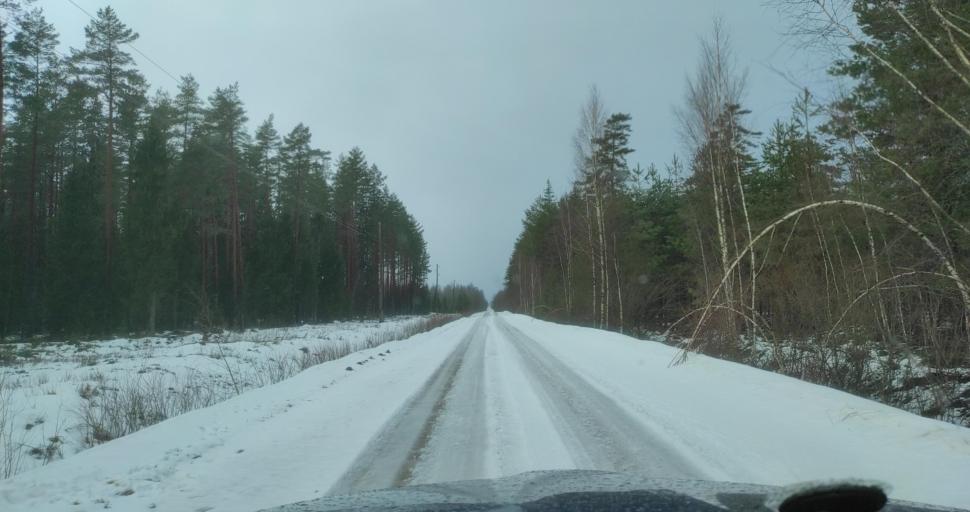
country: LV
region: Dundaga
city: Dundaga
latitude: 57.3852
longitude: 22.1453
